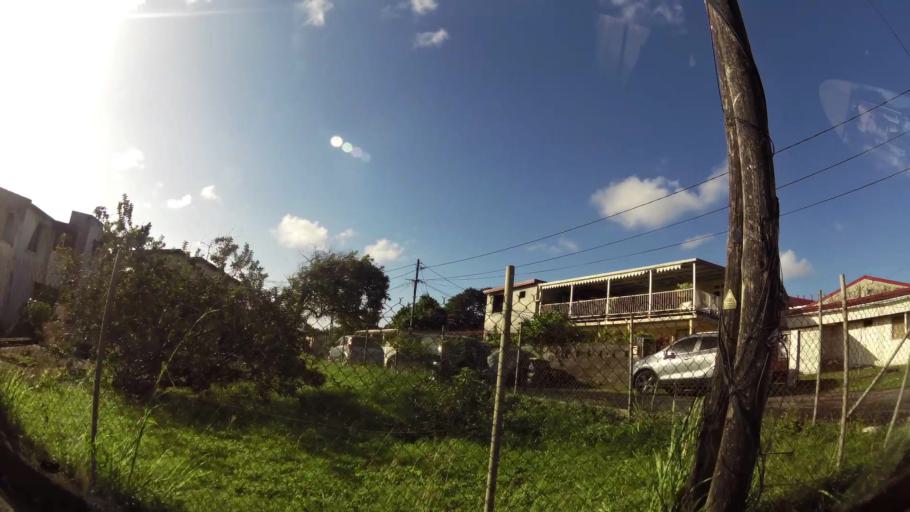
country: MQ
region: Martinique
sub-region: Martinique
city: Le Lamentin
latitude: 14.6284
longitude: -61.0274
